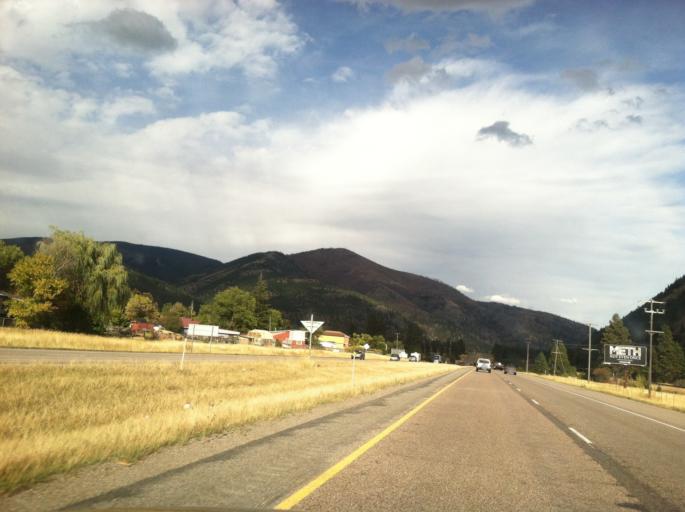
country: US
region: Montana
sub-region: Missoula County
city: East Missoula
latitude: 46.8684
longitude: -113.9436
